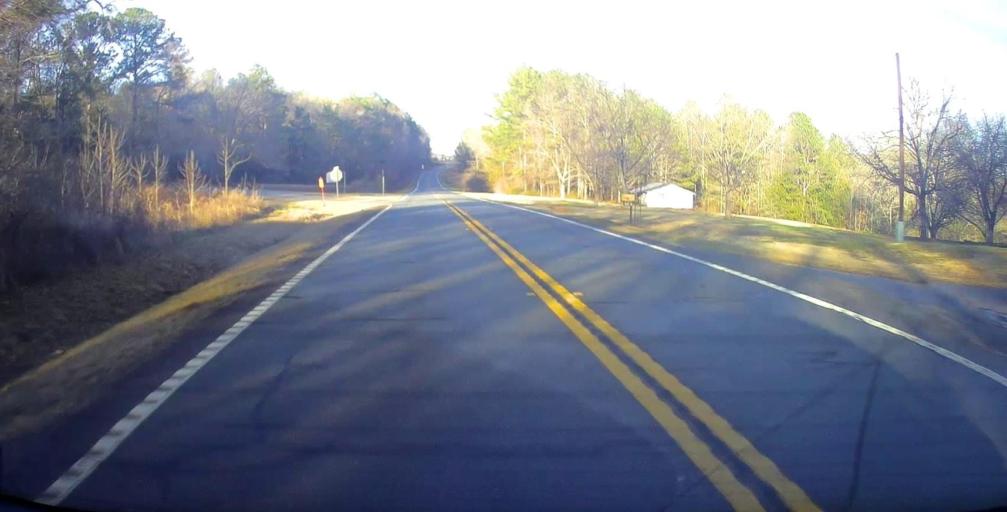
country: US
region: Georgia
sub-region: Talbot County
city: Talbotton
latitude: 32.8036
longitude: -84.4989
